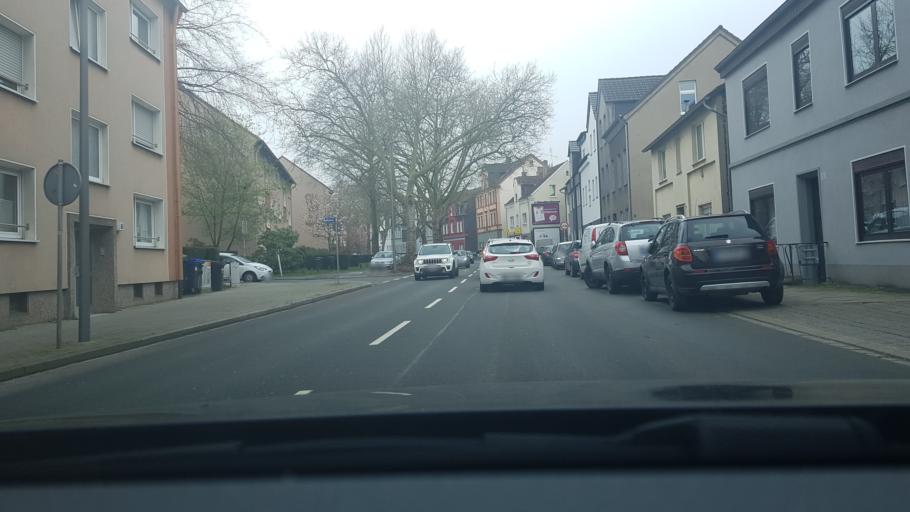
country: DE
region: North Rhine-Westphalia
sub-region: Regierungsbezirk Munster
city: Gelsenkirchen
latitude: 51.4881
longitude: 7.1366
